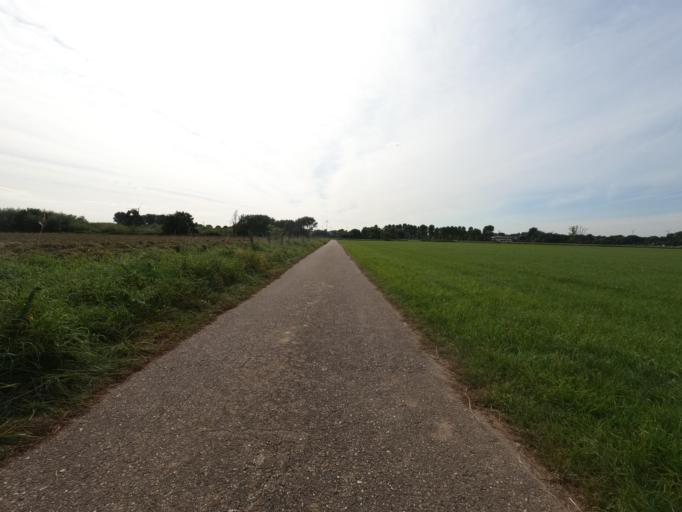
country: DE
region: North Rhine-Westphalia
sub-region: Regierungsbezirk Koln
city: Linnich
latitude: 51.0087
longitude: 6.2539
